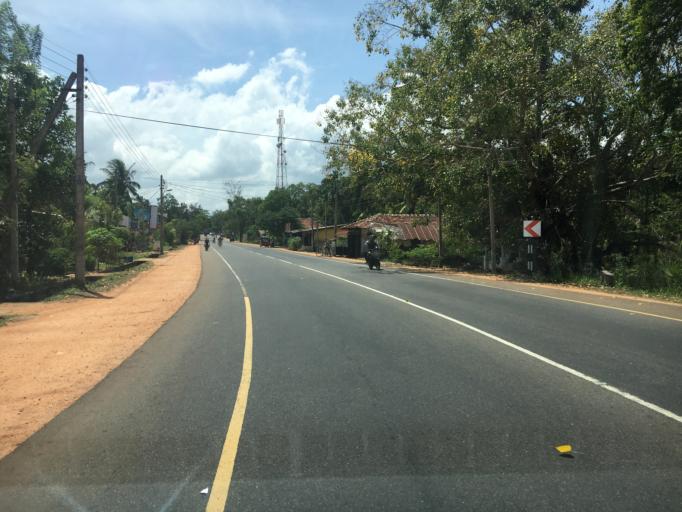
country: LK
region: North Central
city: Anuradhapura
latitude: 8.2725
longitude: 80.5003
